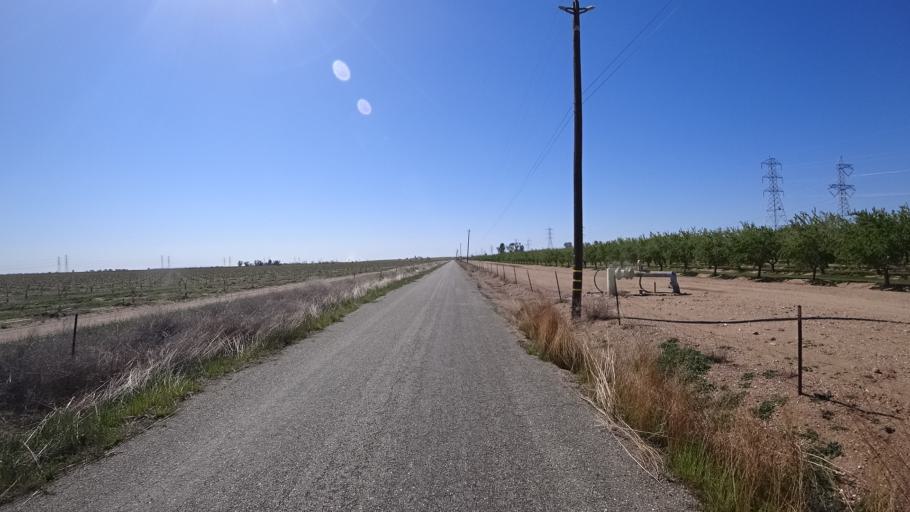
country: US
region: California
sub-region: Glenn County
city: Orland
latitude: 39.6594
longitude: -122.2719
